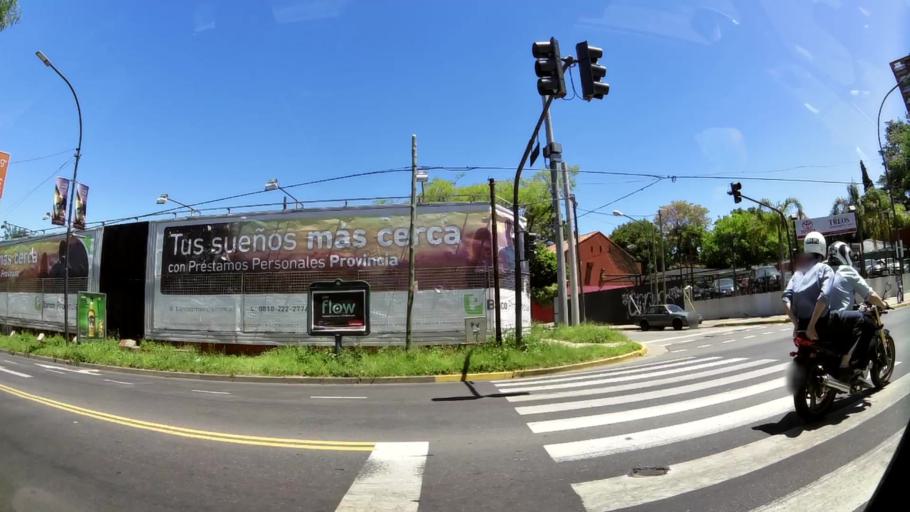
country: AR
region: Buenos Aires
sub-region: Partido de Vicente Lopez
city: Olivos
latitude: -34.4976
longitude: -58.4843
